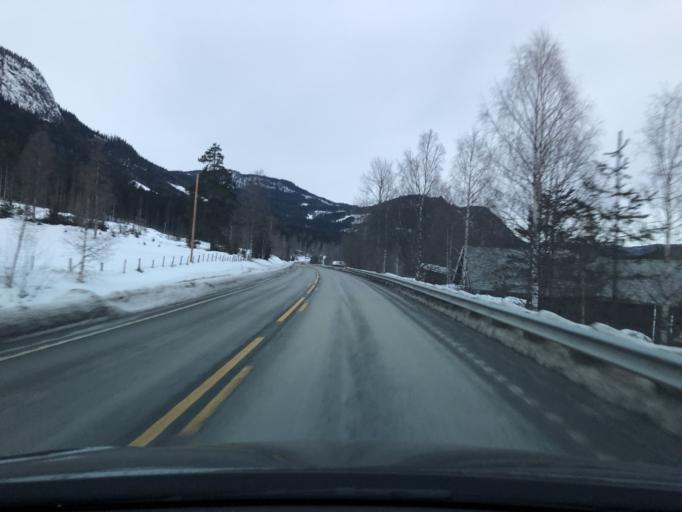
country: NO
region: Oppland
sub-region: Etnedal
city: Bruflat
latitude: 60.7025
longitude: 9.7169
